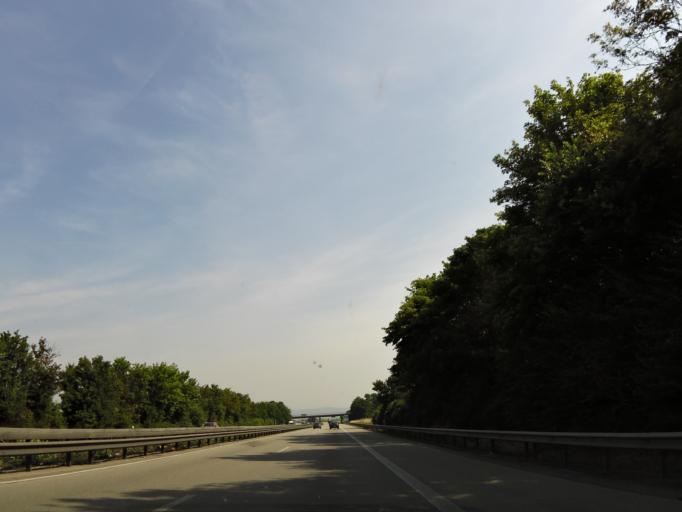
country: DE
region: Rheinland-Pfalz
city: Gensingen
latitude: 49.9022
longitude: 7.9465
